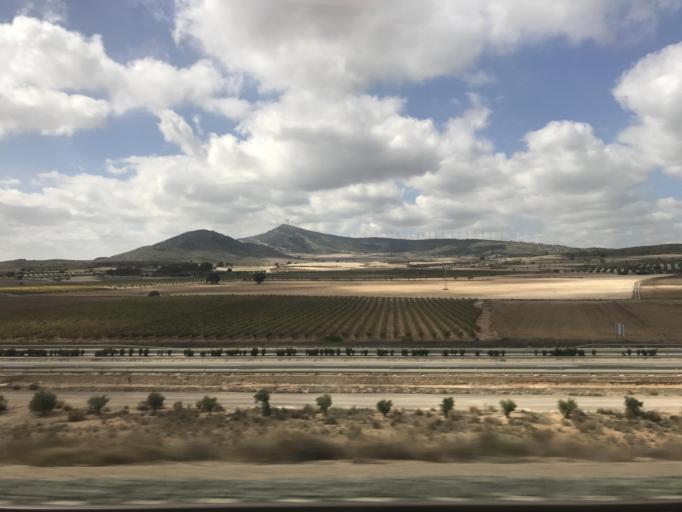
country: ES
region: Castille-La Mancha
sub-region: Provincia de Albacete
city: Caudete
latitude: 38.7664
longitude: -0.9572
